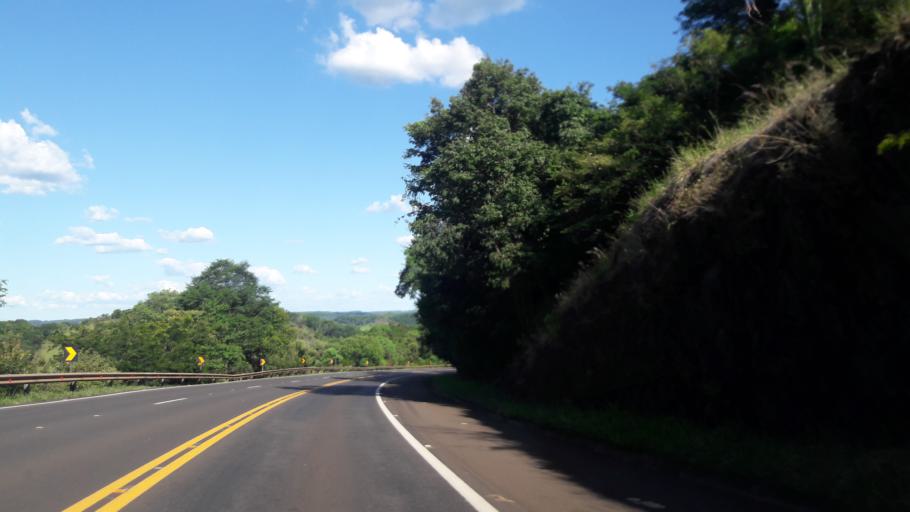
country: BR
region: Parana
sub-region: Laranjeiras Do Sul
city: Laranjeiras do Sul
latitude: -25.4052
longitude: -52.0938
